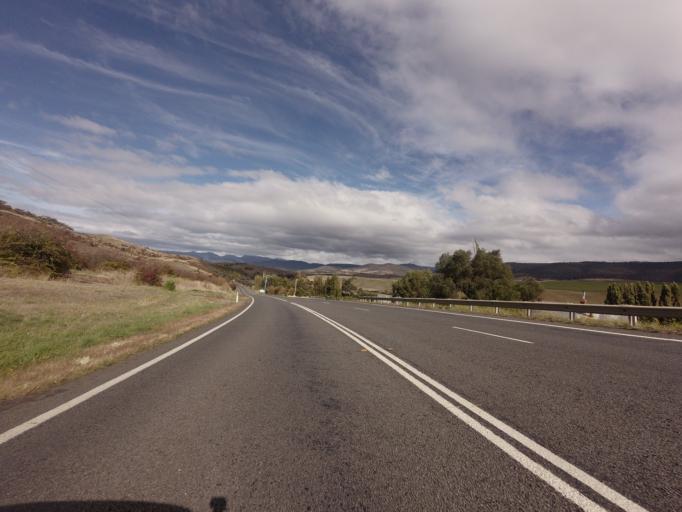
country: AU
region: Tasmania
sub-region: Derwent Valley
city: New Norfolk
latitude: -42.7211
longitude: 146.9487
